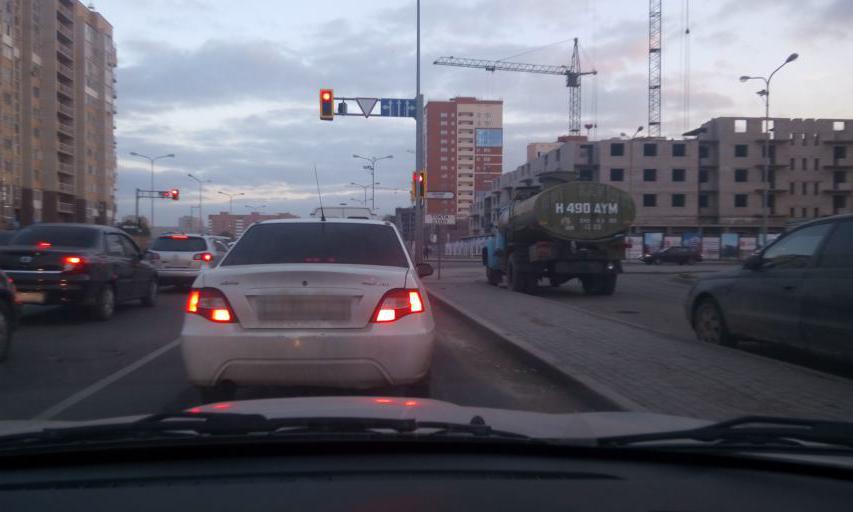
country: KZ
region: Astana Qalasy
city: Astana
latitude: 51.1318
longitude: 71.4951
